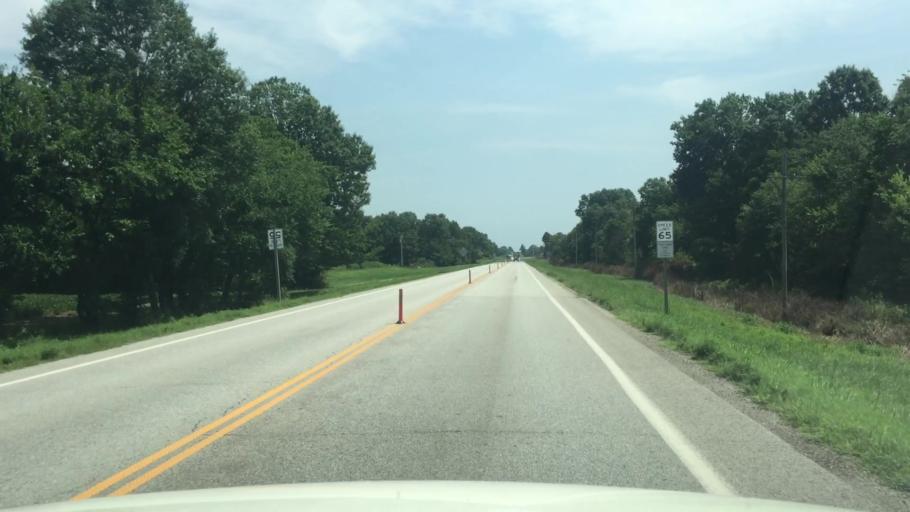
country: US
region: Kansas
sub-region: Cherokee County
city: Columbus
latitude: 37.1781
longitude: -94.8238
